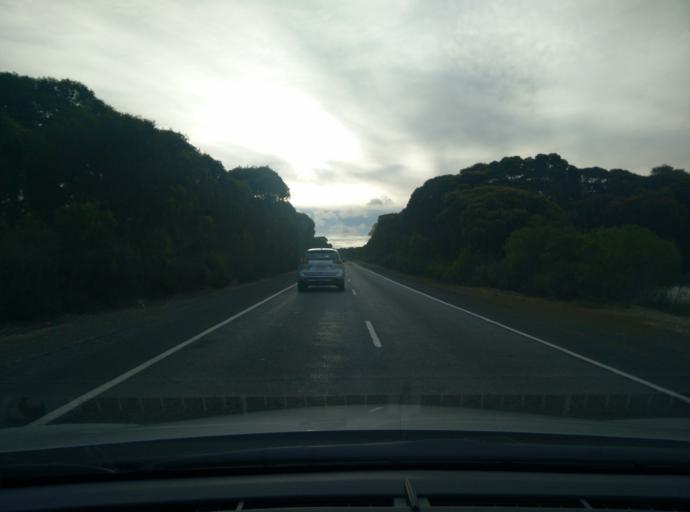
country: AU
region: South Australia
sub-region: Kangaroo Island
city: Kingscote
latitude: -35.8030
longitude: 137.8274
